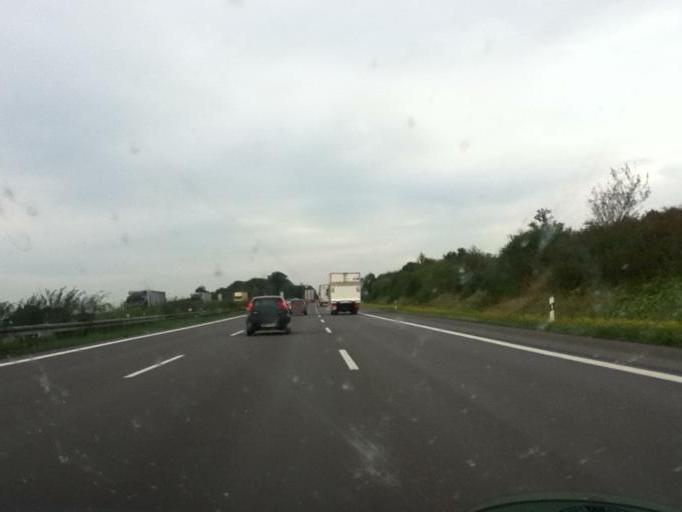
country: DE
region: Saxony
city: Nossen
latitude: 51.0430
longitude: 13.3343
